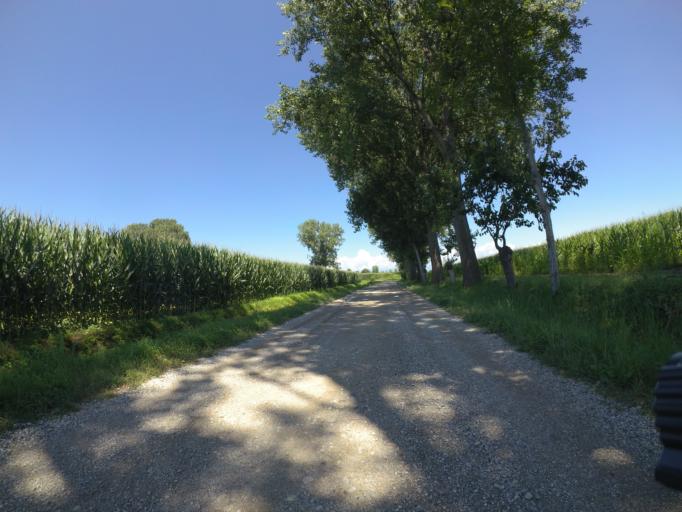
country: IT
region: Friuli Venezia Giulia
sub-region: Provincia di Udine
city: Talmassons
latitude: 45.9163
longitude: 13.1068
